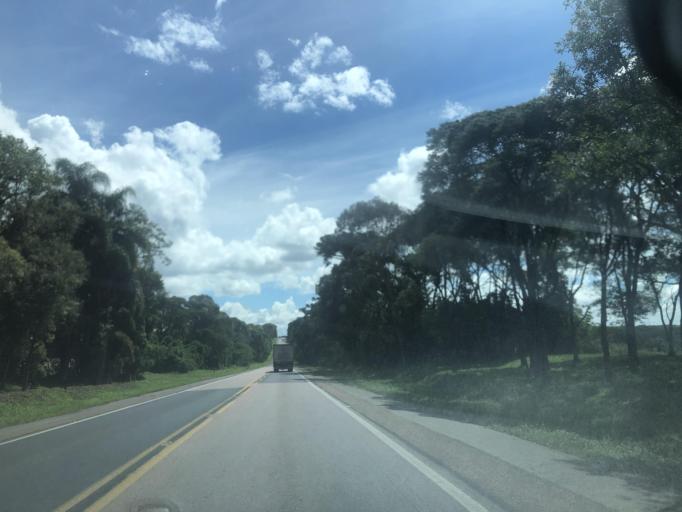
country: BR
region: Santa Catarina
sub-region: Tres Barras
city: Tres Barras
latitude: -26.3382
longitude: -50.0910
